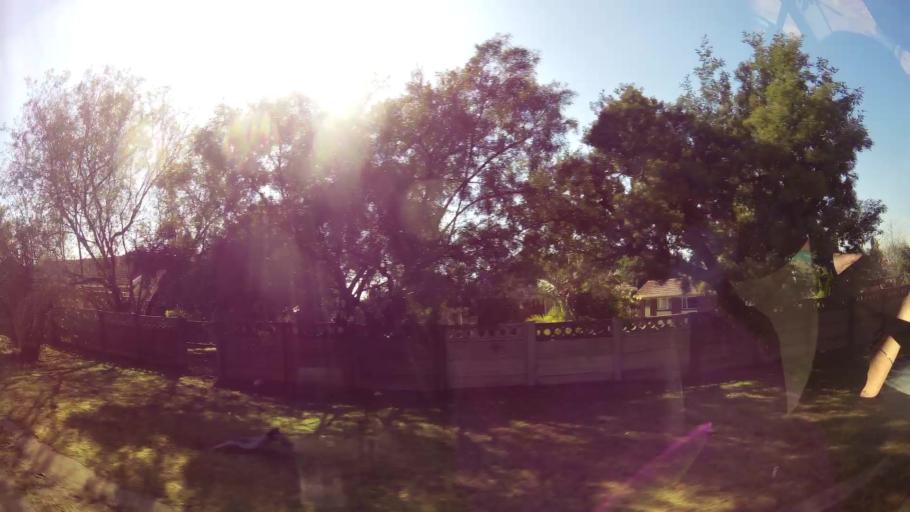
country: ZA
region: Mpumalanga
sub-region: Nkangala District Municipality
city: Witbank
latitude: -25.8729
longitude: 29.2449
